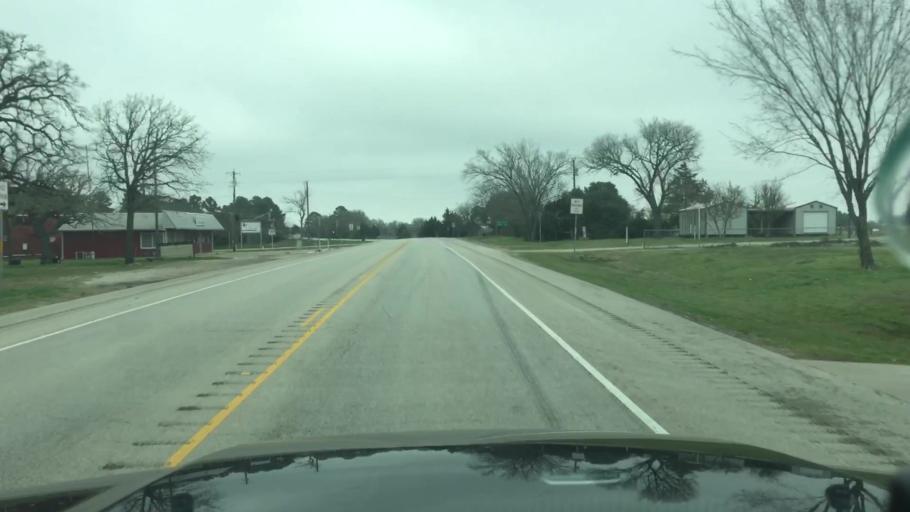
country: US
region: Texas
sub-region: Lee County
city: Giddings
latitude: 30.0544
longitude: -96.9142
